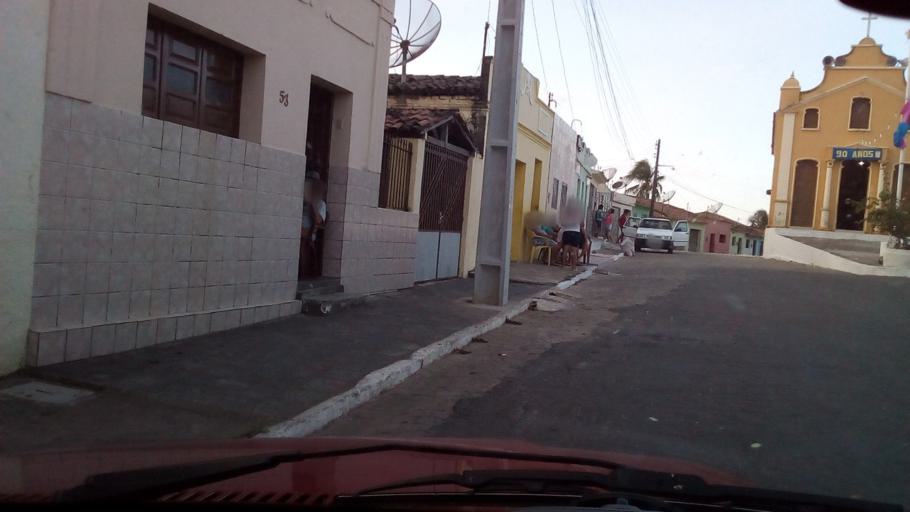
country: BR
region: Paraiba
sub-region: Belem
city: Belem
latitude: -6.7199
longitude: -35.5417
